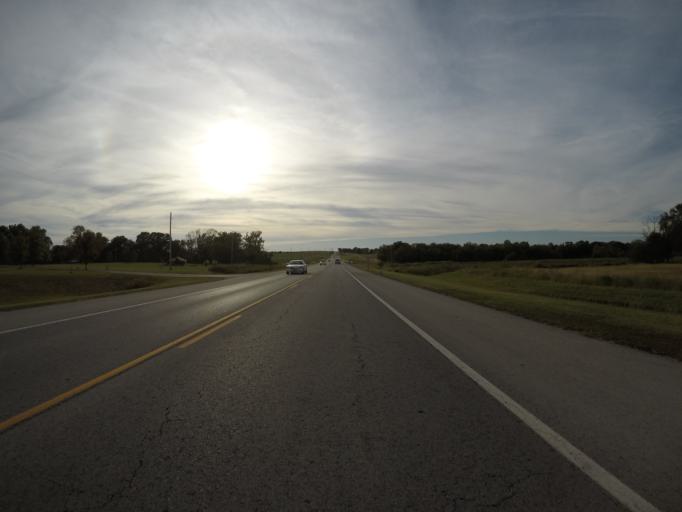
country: US
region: Kansas
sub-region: Douglas County
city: Baldwin City
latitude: 38.7823
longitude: -95.2305
